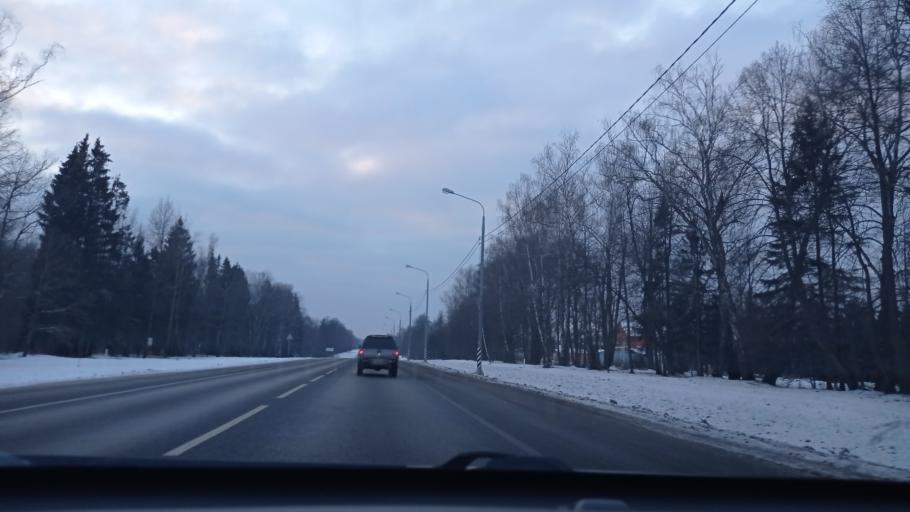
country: RU
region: Moskovskaya
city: Kievskij
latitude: 55.2363
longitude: 37.0362
